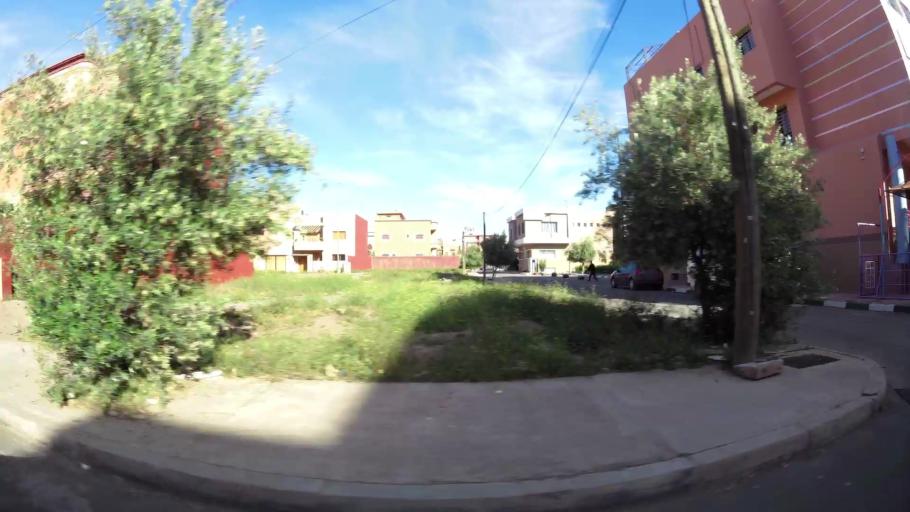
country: MA
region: Marrakech-Tensift-Al Haouz
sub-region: Marrakech
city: Marrakesh
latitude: 31.6850
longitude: -8.0655
